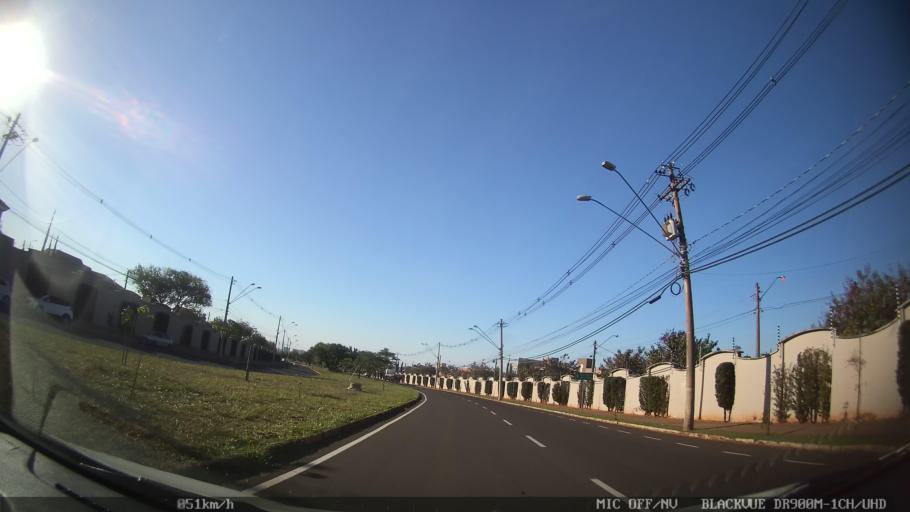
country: BR
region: Sao Paulo
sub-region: Sao Jose Do Rio Preto
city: Sao Jose do Rio Preto
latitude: -20.8625
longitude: -49.4120
